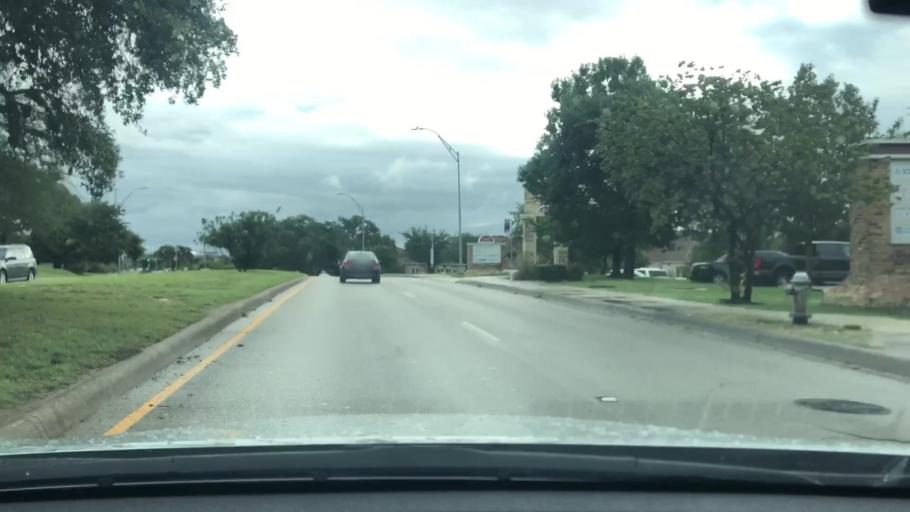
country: US
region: Texas
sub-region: Bexar County
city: Hollywood Park
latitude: 29.6143
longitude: -98.4760
